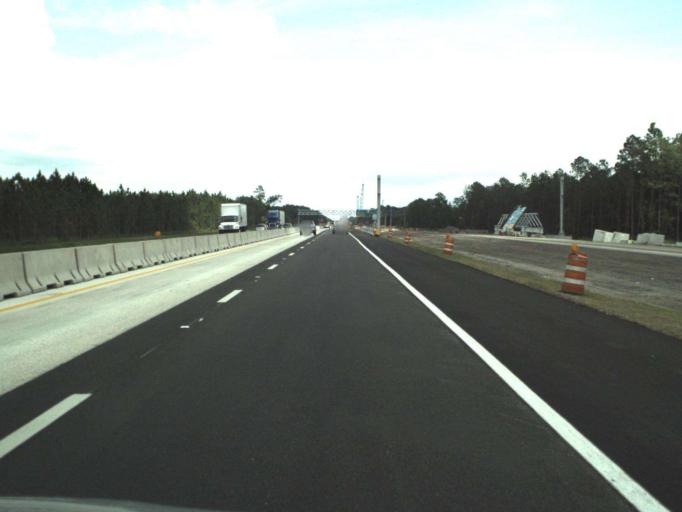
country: US
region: Florida
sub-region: Volusia County
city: South Daytona
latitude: 29.1459
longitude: -81.0983
